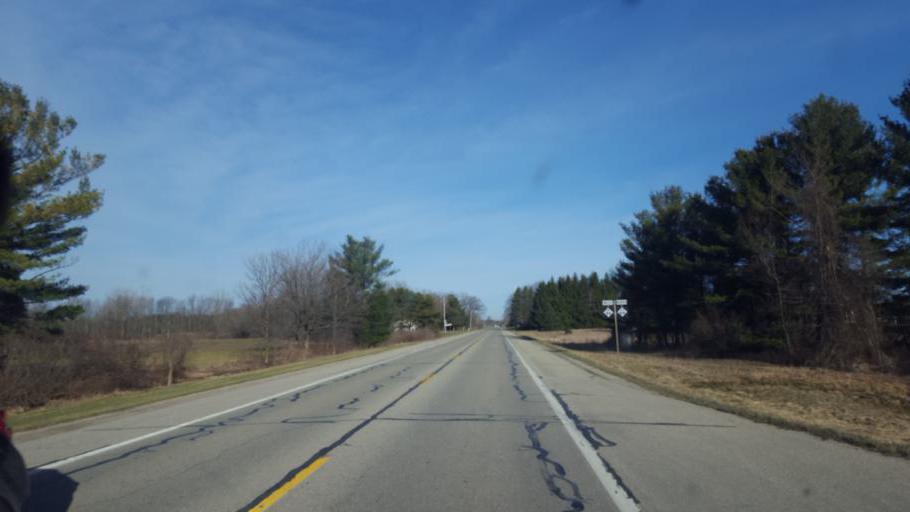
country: US
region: Michigan
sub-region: Montcalm County
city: Edmore
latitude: 43.4133
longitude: -85.1246
